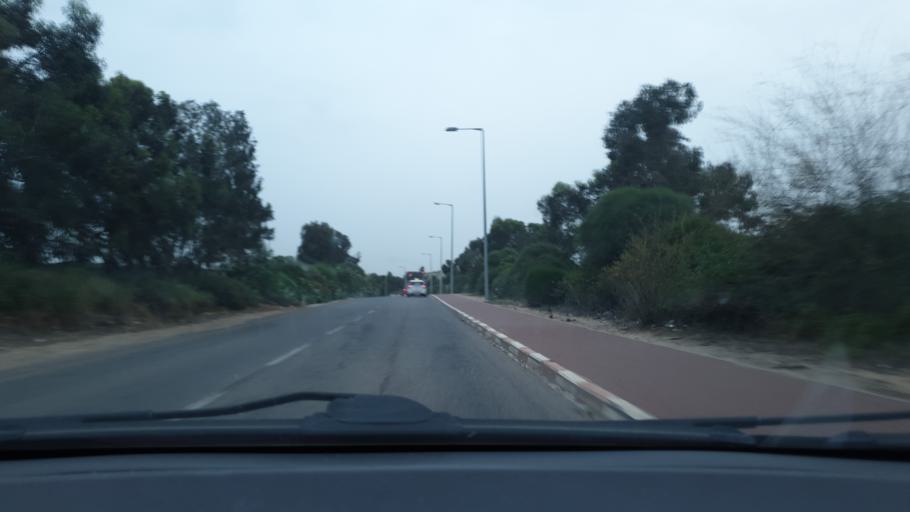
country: IL
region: Central District
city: Kefar Habad
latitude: 31.9831
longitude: 34.8409
